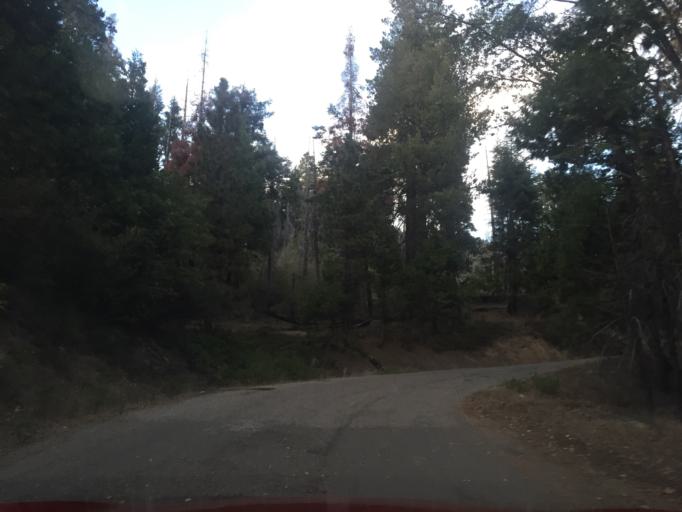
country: US
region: California
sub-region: Tulare County
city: Three Rivers
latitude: 36.4518
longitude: -118.6896
